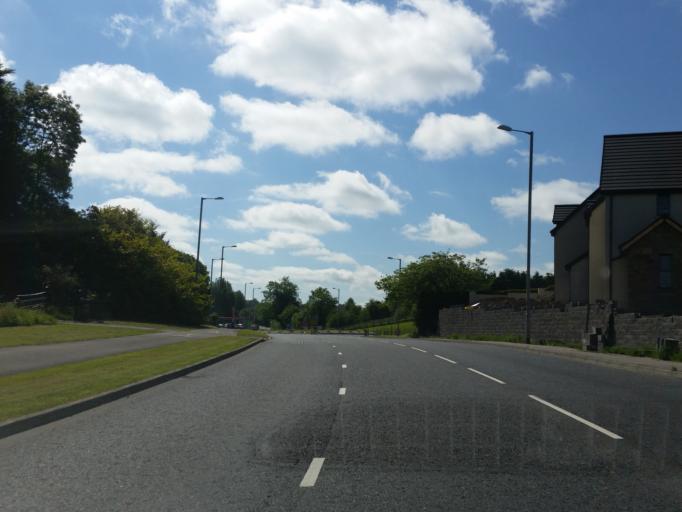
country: GB
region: Northern Ireland
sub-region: Fermanagh District
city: Enniskillen
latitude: 54.3616
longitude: -7.6353
